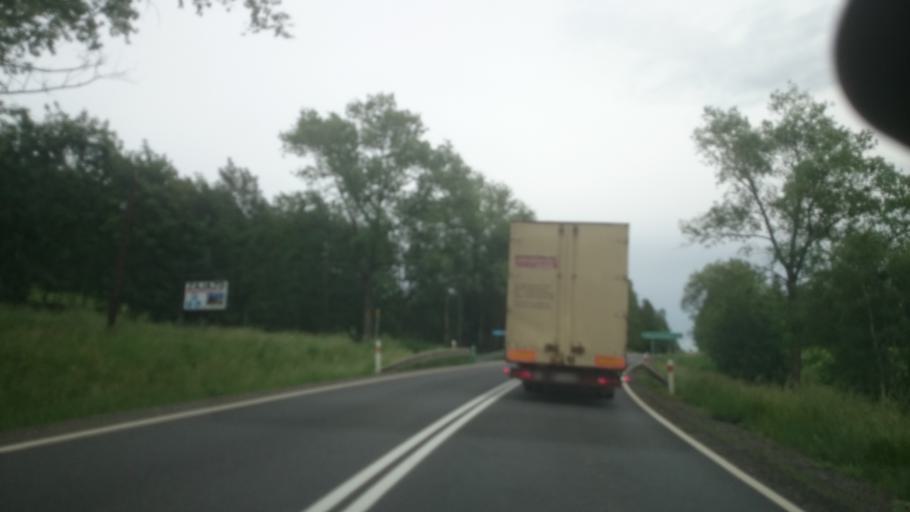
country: PL
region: Lower Silesian Voivodeship
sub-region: Powiat klodzki
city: Klodzko
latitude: 50.4340
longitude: 16.7086
